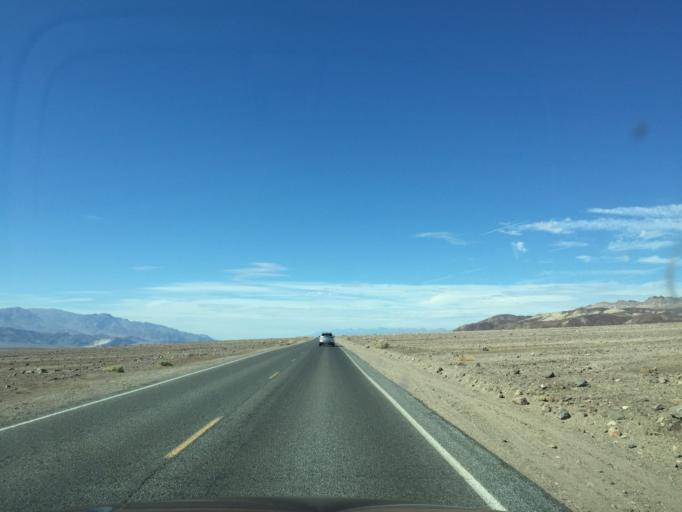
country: US
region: Nevada
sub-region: Nye County
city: Beatty
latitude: 36.2926
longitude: -116.8083
